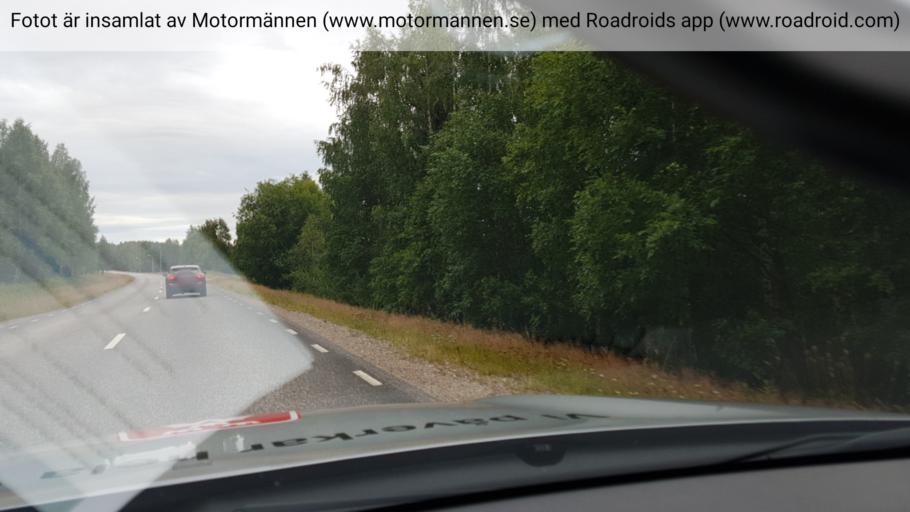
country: SE
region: Norrbotten
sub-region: Overkalix Kommun
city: OEverkalix
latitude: 66.5411
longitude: 22.7538
